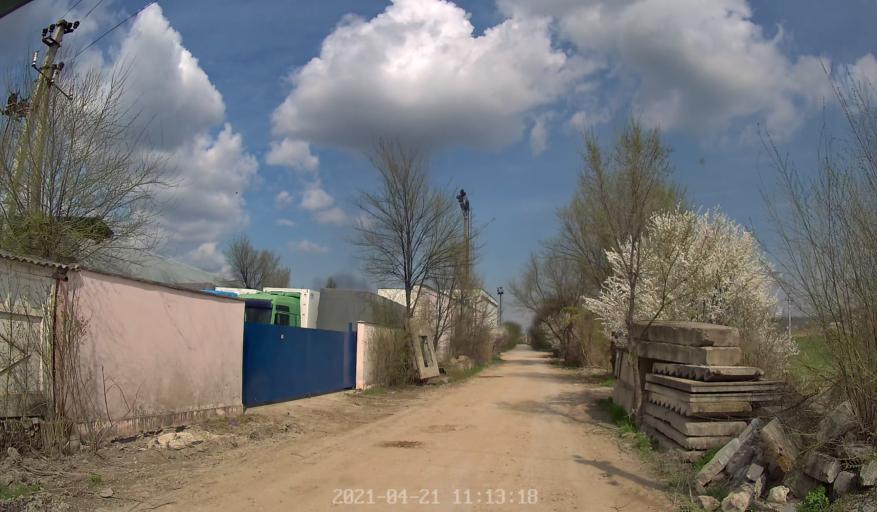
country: MD
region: Chisinau
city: Singera
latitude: 46.9557
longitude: 28.9317
